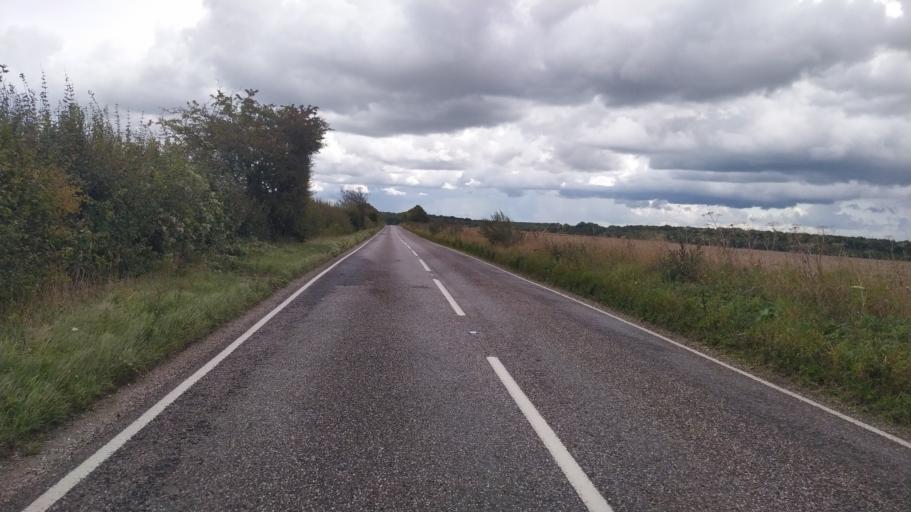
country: GB
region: England
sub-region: Wiltshire
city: Bower Chalke
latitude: 50.9459
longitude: -1.9787
